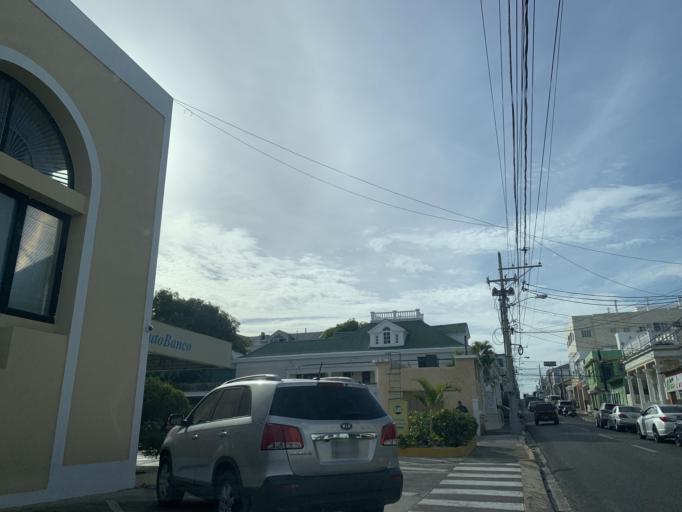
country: DO
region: Puerto Plata
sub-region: Puerto Plata
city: Puerto Plata
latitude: 19.7970
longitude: -70.6912
